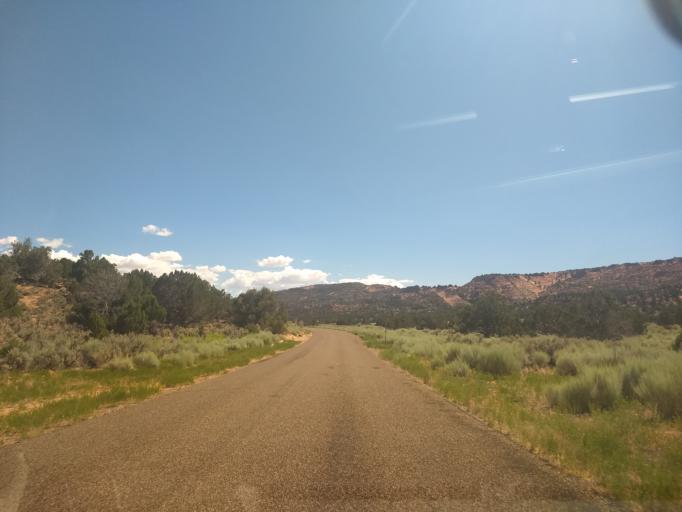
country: US
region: Utah
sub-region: Washington County
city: Hildale
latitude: 37.0020
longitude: -112.8603
